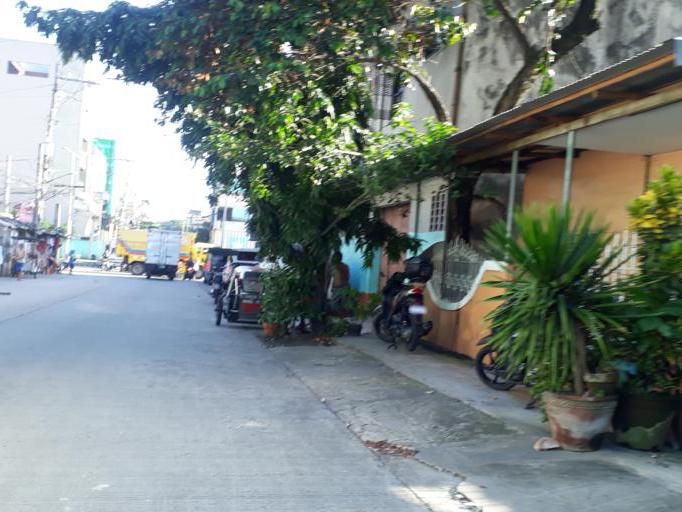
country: PH
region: Metro Manila
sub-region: Caloocan City
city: Niugan
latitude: 14.6453
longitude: 120.9792
